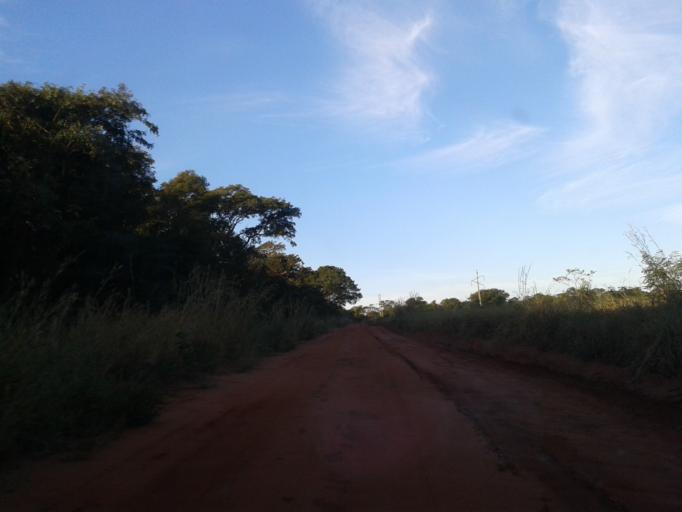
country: BR
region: Minas Gerais
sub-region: Santa Vitoria
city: Santa Vitoria
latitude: -19.0096
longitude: -50.3761
